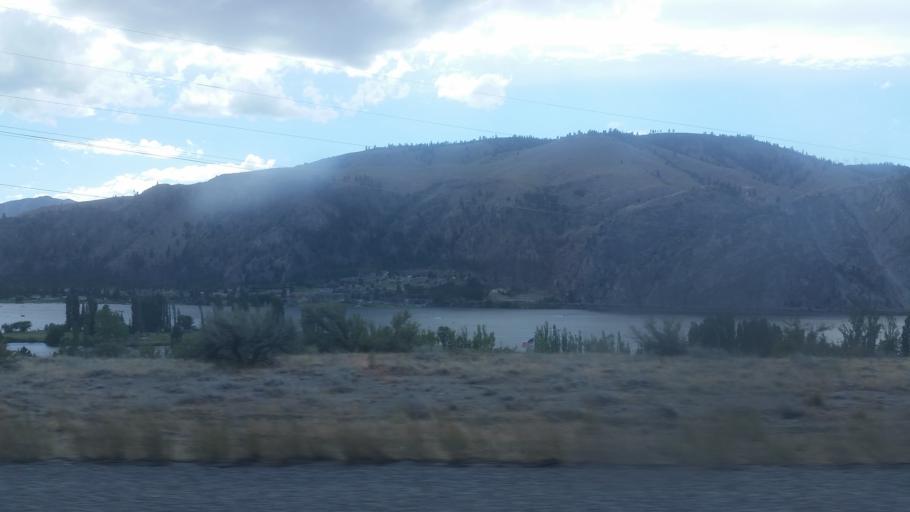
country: US
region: Washington
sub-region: Chelan County
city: Entiat
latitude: 47.7094
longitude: -120.1963
